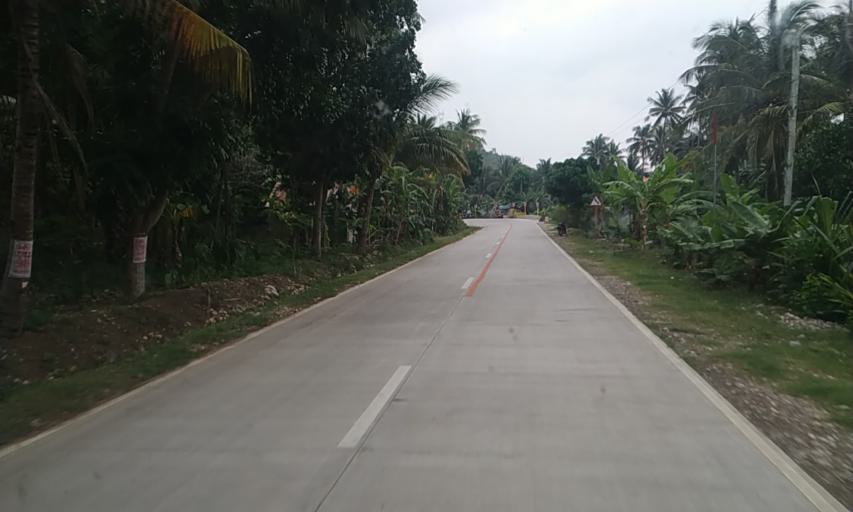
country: PH
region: Central Visayas
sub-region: Province of Negros Oriental
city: Calamba
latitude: 10.1933
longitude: 123.2949
